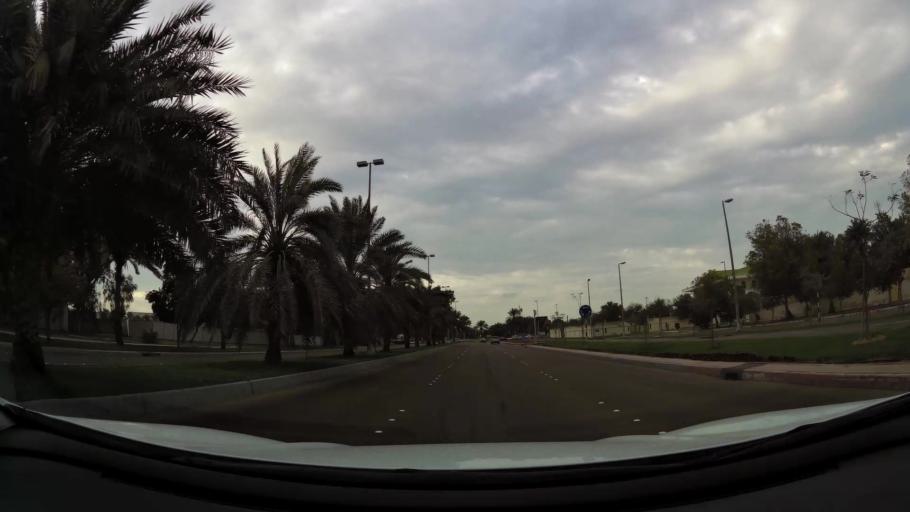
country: AE
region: Abu Dhabi
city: Abu Dhabi
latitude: 24.4343
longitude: 54.3676
